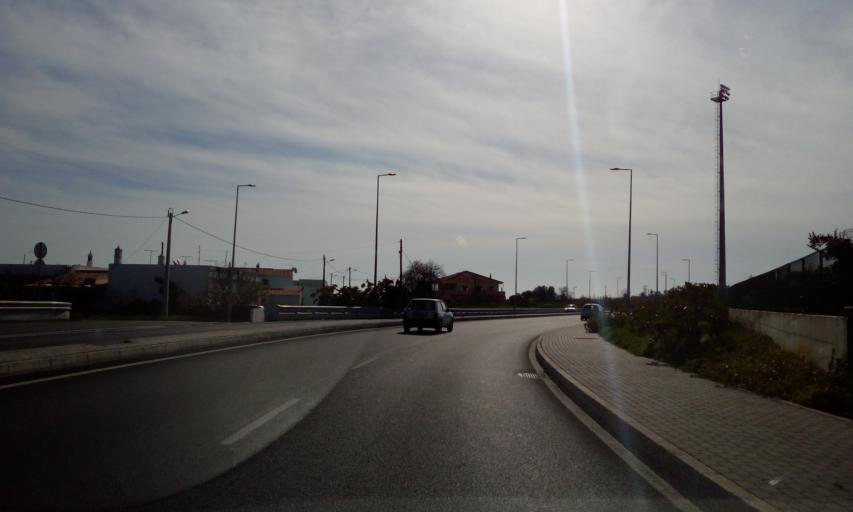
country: PT
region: Faro
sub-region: Faro
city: Faro
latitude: 37.0291
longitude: -7.9159
